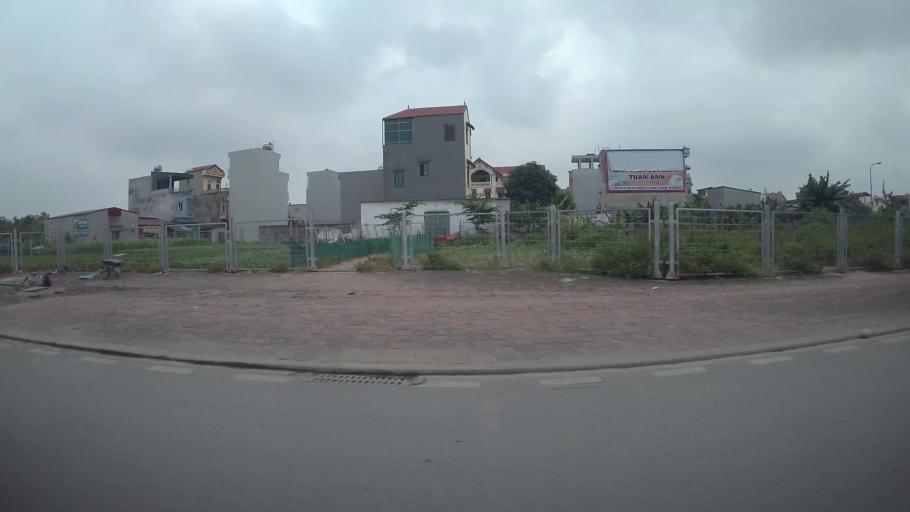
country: VN
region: Ha Noi
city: Trau Quy
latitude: 21.0532
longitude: 105.9201
